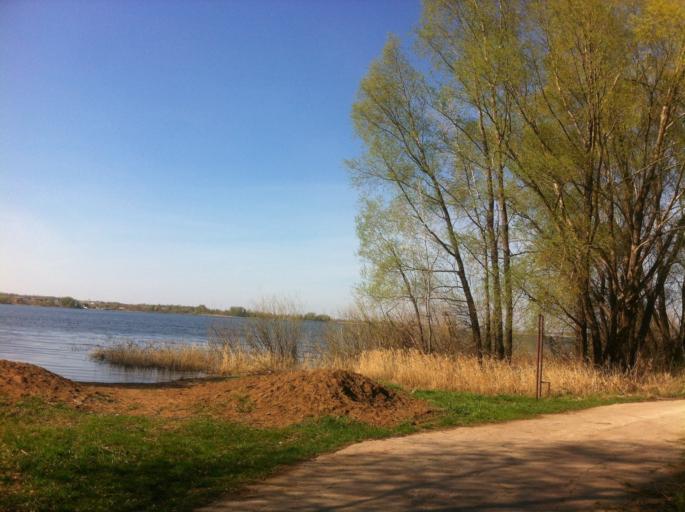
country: RU
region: Samara
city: Smyshlyayevka
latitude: 53.1200
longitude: 50.4116
